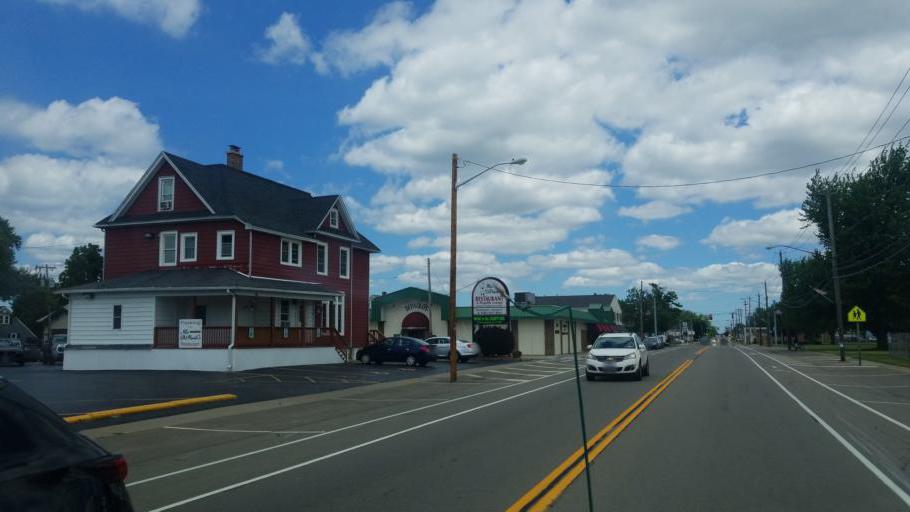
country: US
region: New York
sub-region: Erie County
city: Blasdell
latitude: 42.7944
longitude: -78.8238
